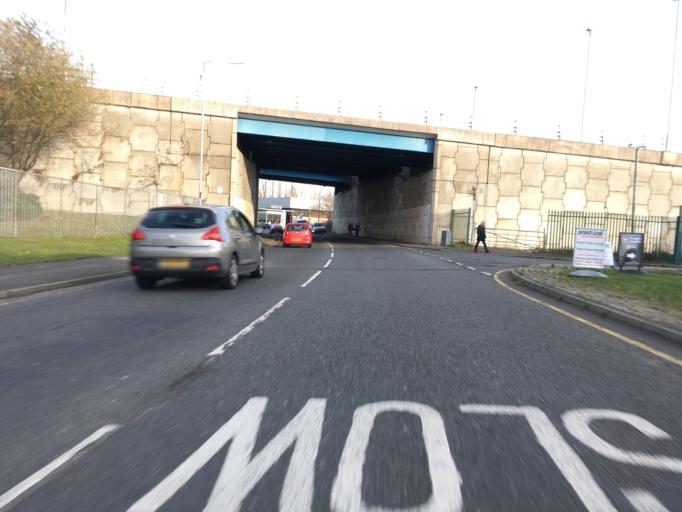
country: GB
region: England
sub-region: Borough of Stockport
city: Cheadle Hulme
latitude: 53.3564
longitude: -2.2036
